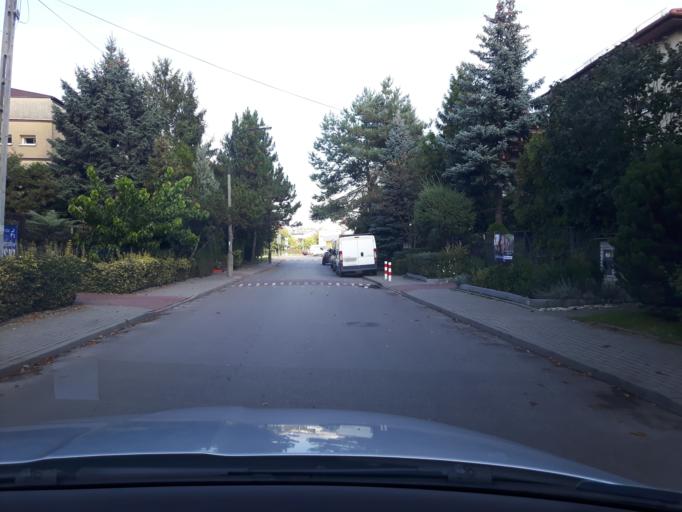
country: PL
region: Masovian Voivodeship
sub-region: Powiat wolominski
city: Zabki
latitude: 52.2805
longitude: 21.0781
